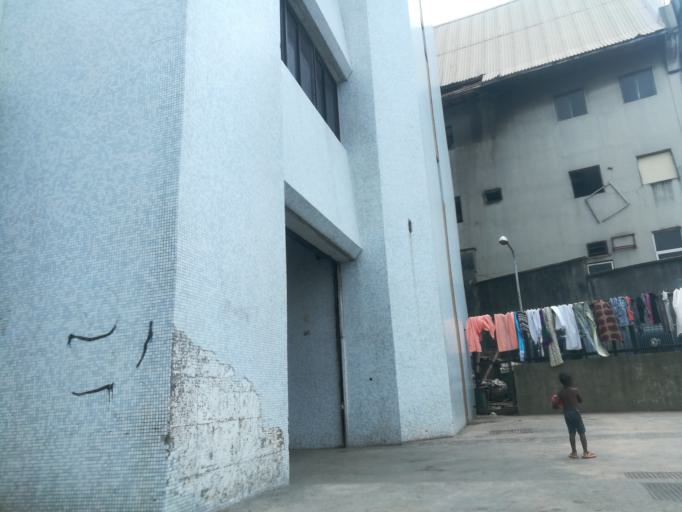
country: NG
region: Lagos
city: Lagos
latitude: 6.4571
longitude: 3.3802
